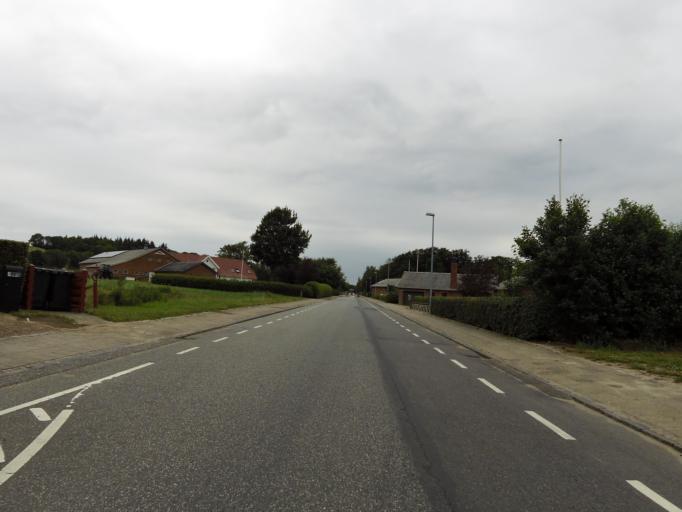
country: DK
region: South Denmark
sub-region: Tonder Kommune
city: Logumkloster
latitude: 55.0787
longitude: 8.9312
